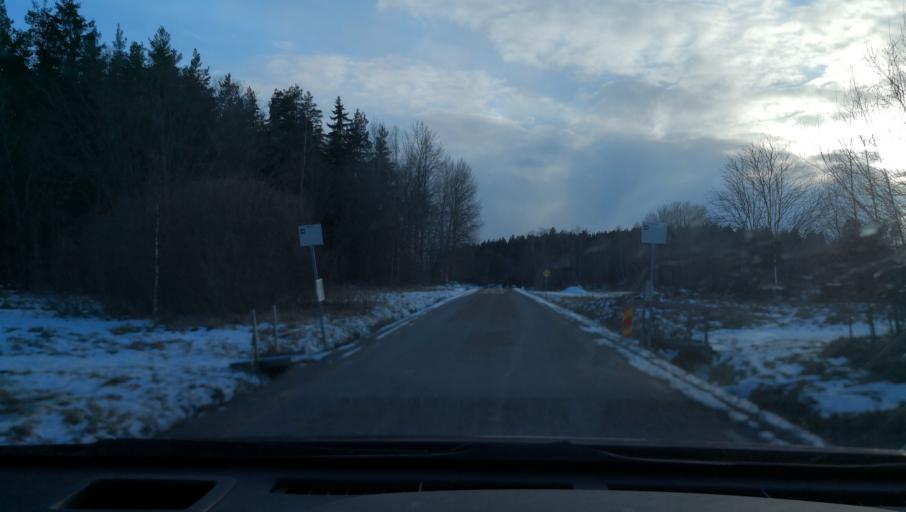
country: SE
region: Vaestmanland
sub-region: Vasteras
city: Tillberga
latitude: 59.6503
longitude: 16.7516
